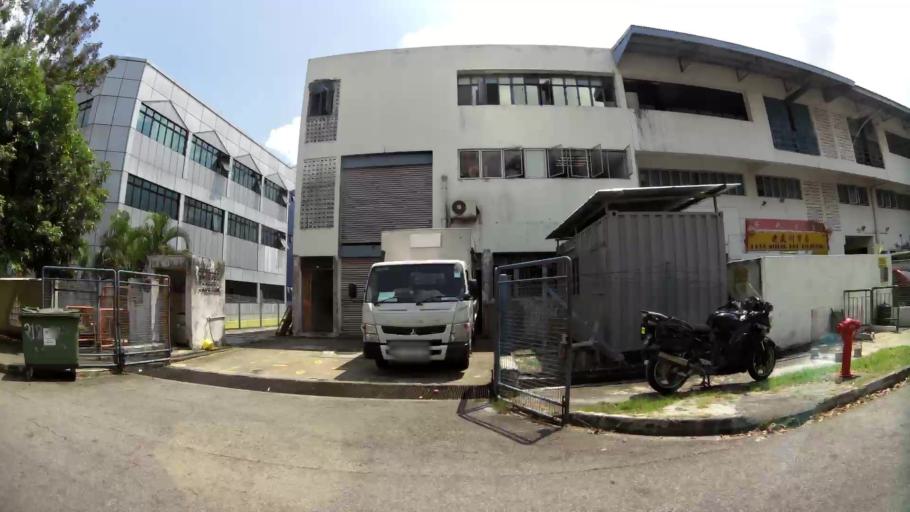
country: MY
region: Johor
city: Kampung Pasir Gudang Baru
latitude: 1.3874
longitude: 103.8301
